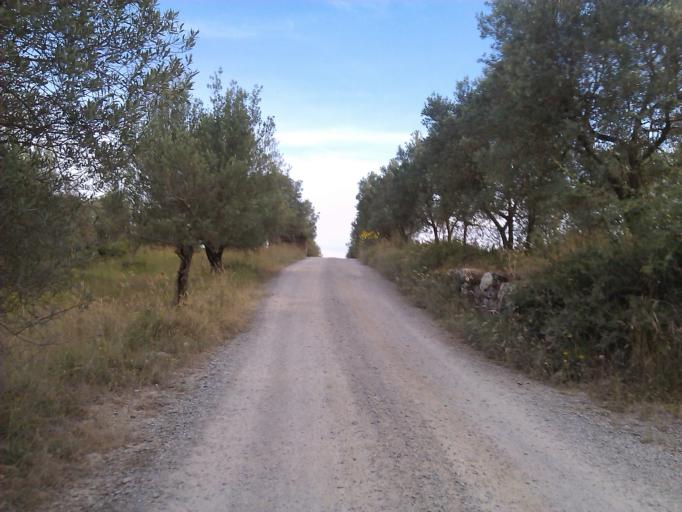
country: IT
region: Tuscany
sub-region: Province of Arezzo
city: Ponticino
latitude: 43.4674
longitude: 11.7294
